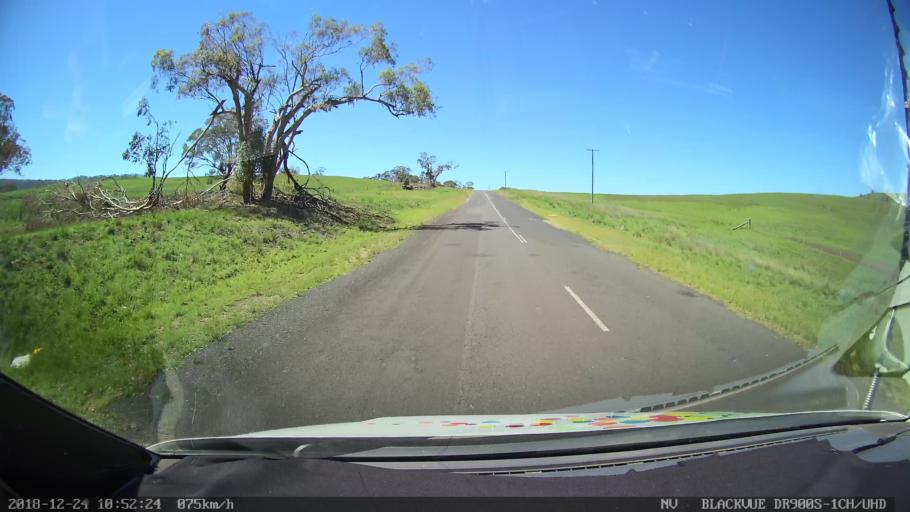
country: AU
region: New South Wales
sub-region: Upper Hunter Shire
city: Merriwa
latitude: -31.9800
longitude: 150.4220
